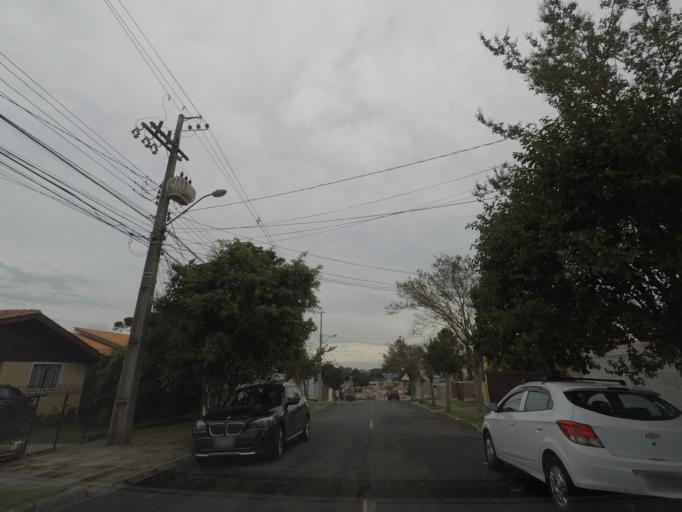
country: BR
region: Parana
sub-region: Curitiba
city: Curitiba
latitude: -25.4658
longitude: -49.3033
